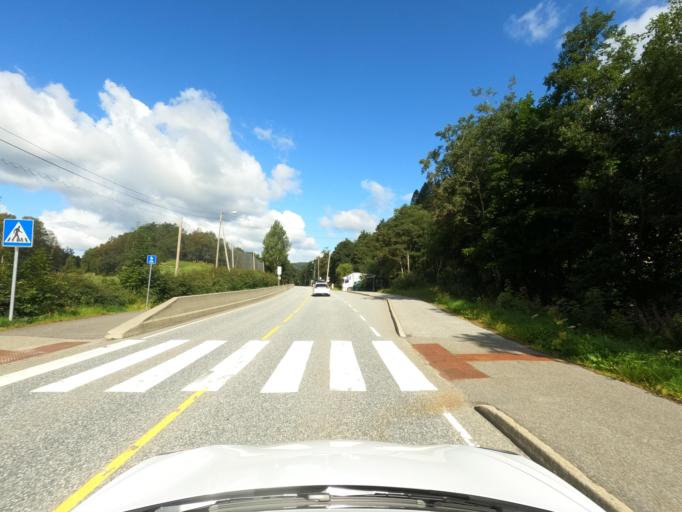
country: NO
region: Hordaland
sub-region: Bergen
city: Bergen
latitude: 60.4449
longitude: 5.3255
